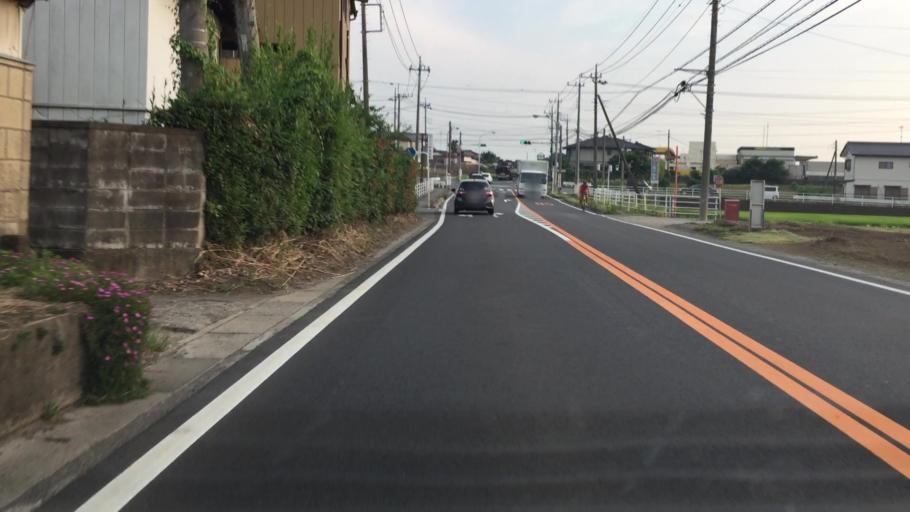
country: JP
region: Tochigi
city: Fujioka
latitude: 36.2837
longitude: 139.6647
